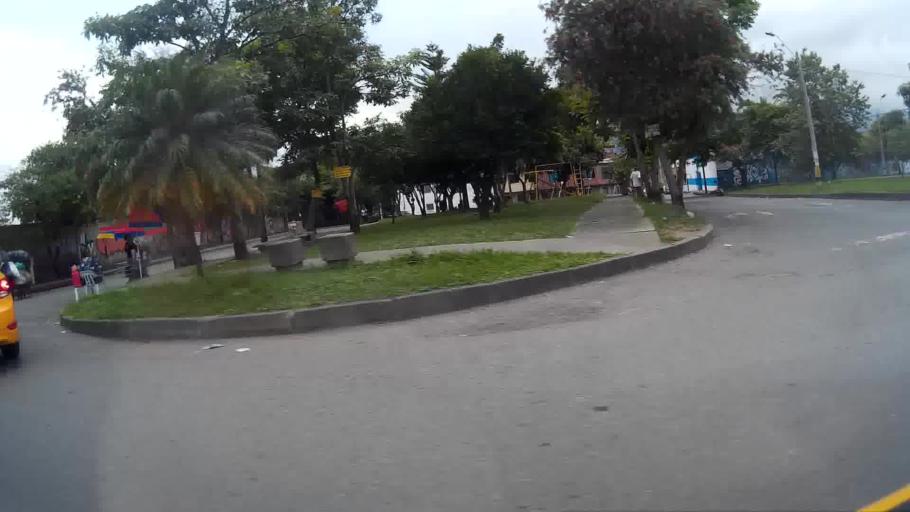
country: CO
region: Antioquia
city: Medellin
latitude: 6.2289
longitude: -75.5872
